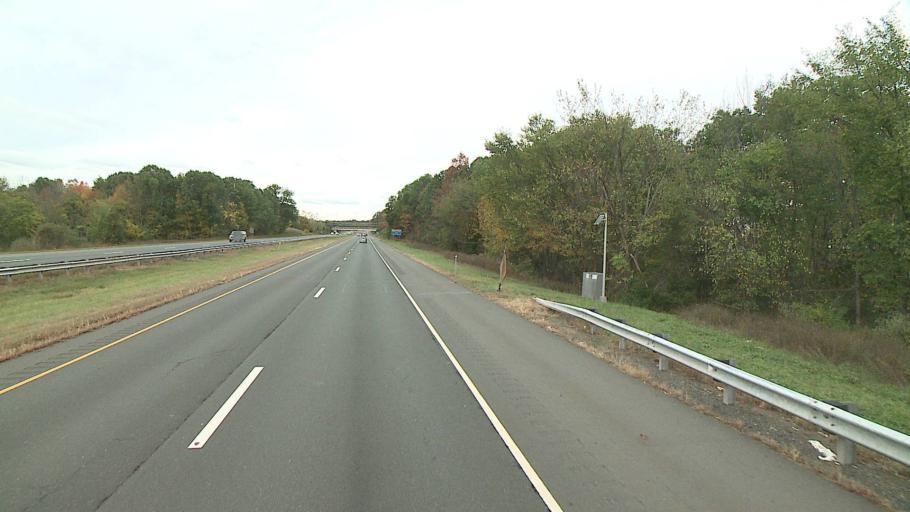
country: US
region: Connecticut
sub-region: Hartford County
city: Kensington
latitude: 41.6248
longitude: -72.7189
